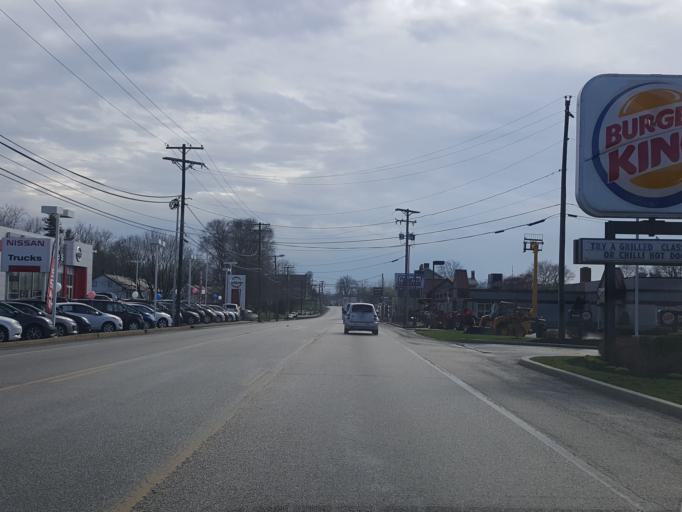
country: US
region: Pennsylvania
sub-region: Lebanon County
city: Pleasant Hill
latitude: 40.3388
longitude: -76.4479
